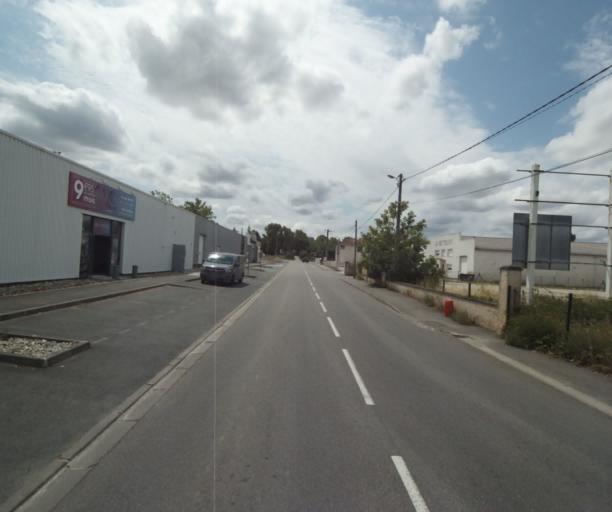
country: FR
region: Midi-Pyrenees
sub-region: Departement de la Haute-Garonne
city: Revel
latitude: 43.4556
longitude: 1.9941
